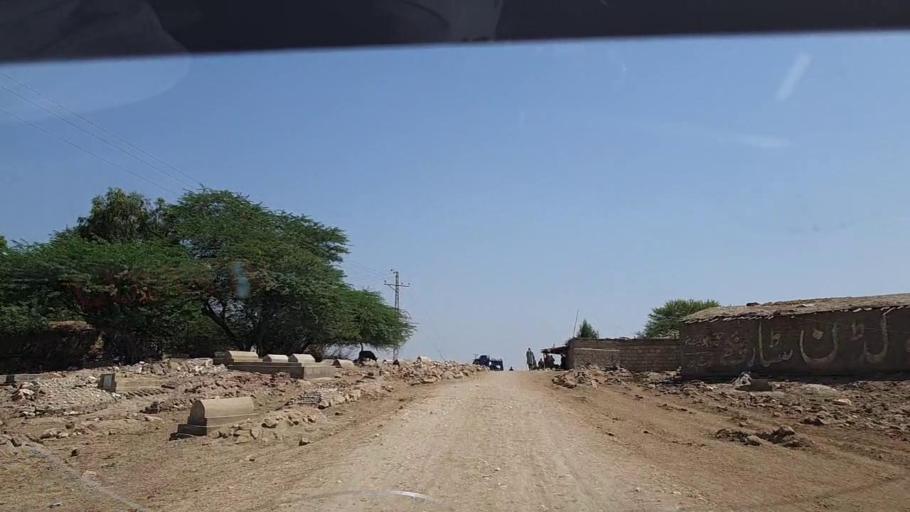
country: PK
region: Sindh
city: Ghauspur
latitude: 28.1346
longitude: 69.0856
